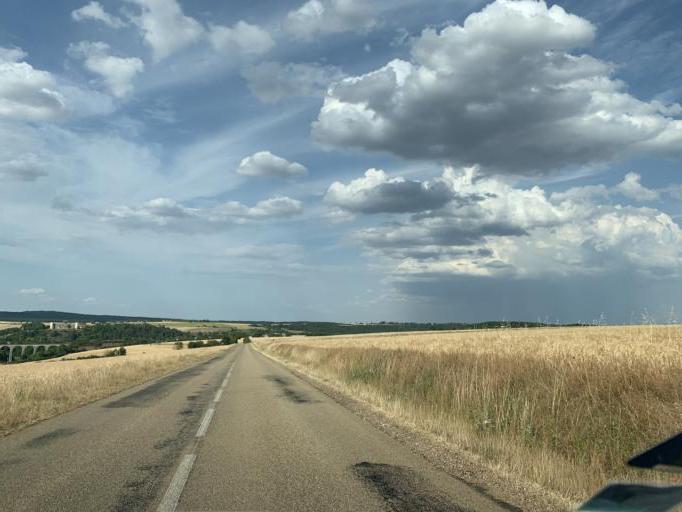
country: FR
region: Bourgogne
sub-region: Departement de l'Yonne
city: Fontenailles
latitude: 47.5378
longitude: 3.4111
